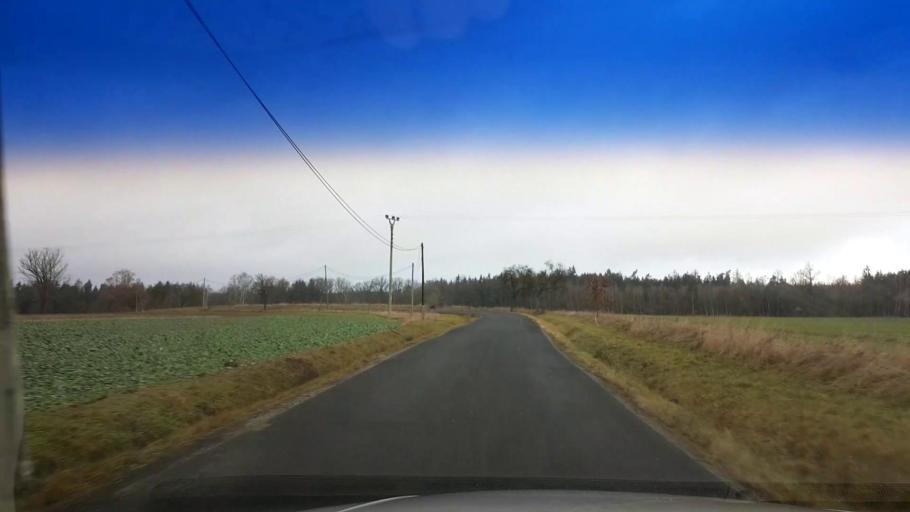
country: CZ
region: Karlovarsky
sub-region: Okres Cheb
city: Cheb
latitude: 50.0401
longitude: 12.3655
